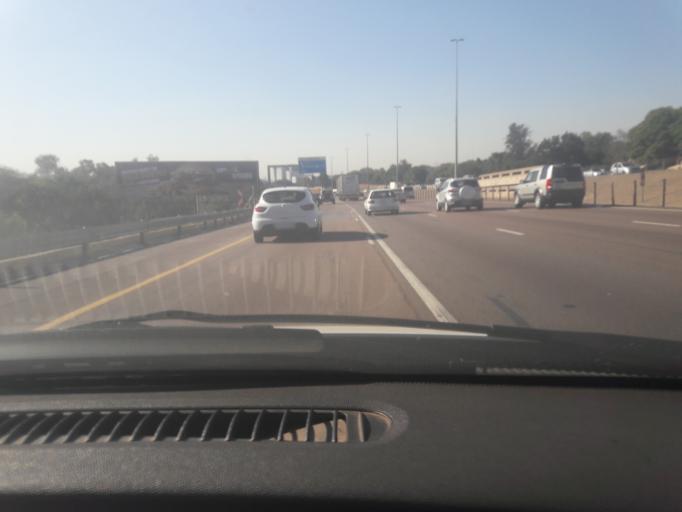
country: ZA
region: Gauteng
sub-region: City of Tshwane Metropolitan Municipality
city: Pretoria
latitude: -25.7940
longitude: 28.2665
